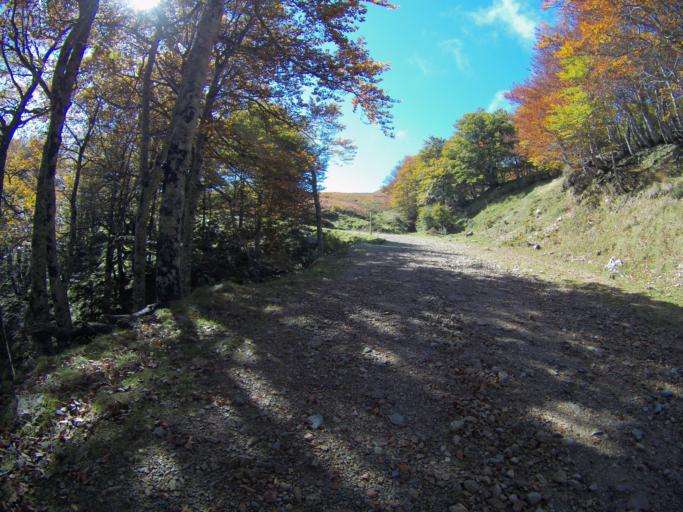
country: ES
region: Navarre
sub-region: Provincia de Navarra
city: Orbara
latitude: 43.0357
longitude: -1.2918
